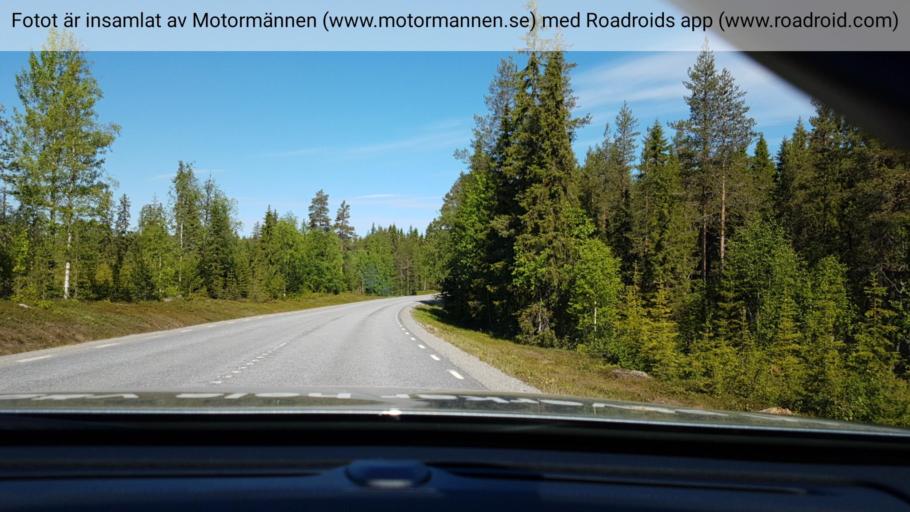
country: SE
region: Vaesterbotten
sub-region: Bjurholms Kommun
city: Bjurholm
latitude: 63.9609
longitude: 18.8563
